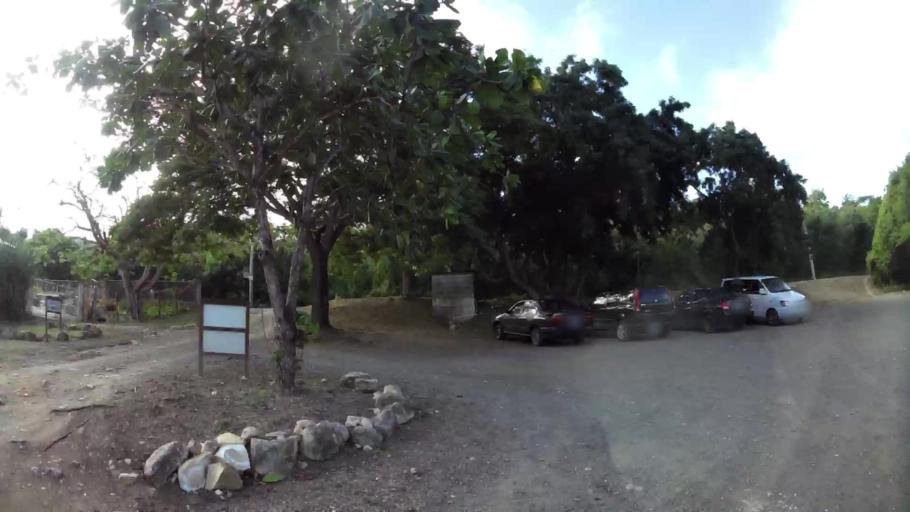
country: AG
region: Saint Peter
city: Parham
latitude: 17.0960
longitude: -61.7250
